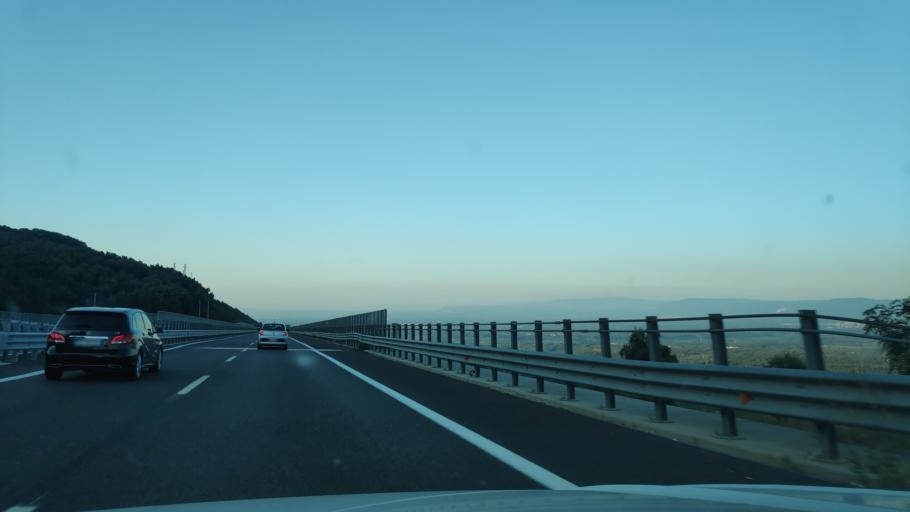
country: IT
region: Calabria
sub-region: Provincia di Reggio Calabria
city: Seminara
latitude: 38.3360
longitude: 15.8618
